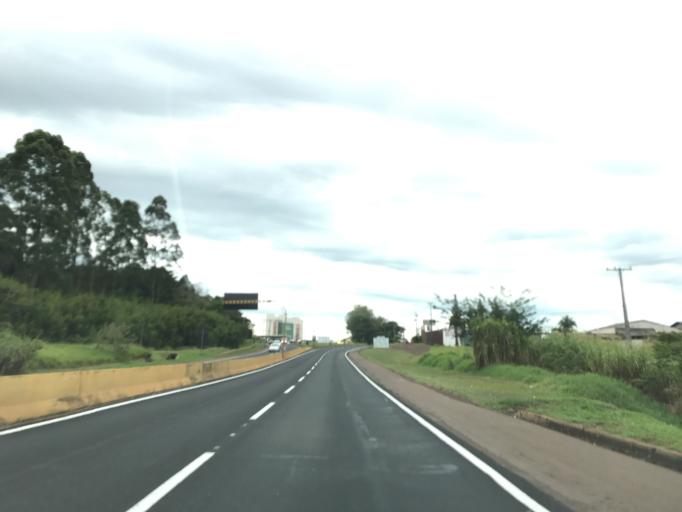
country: BR
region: Parana
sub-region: Rolandia
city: Rolandia
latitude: -23.3592
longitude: -51.3974
